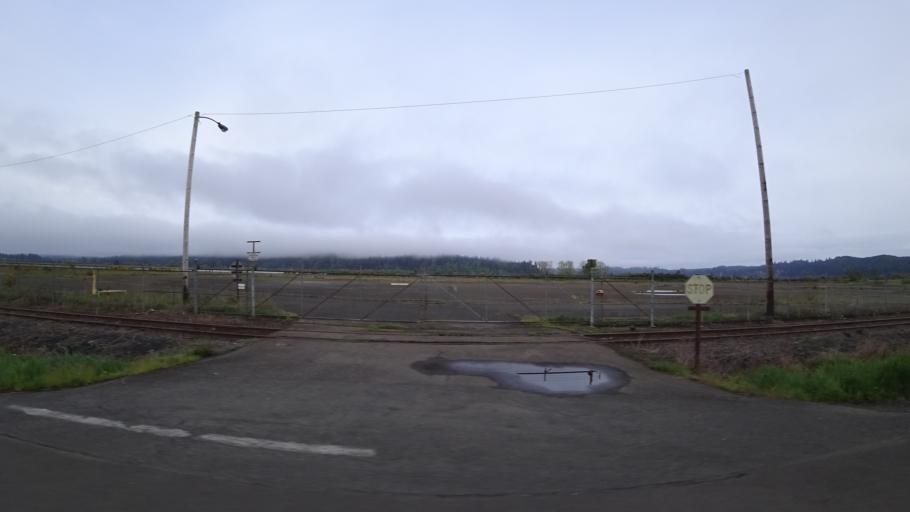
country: US
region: Oregon
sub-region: Douglas County
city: Reedsport
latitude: 43.7326
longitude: -124.1115
